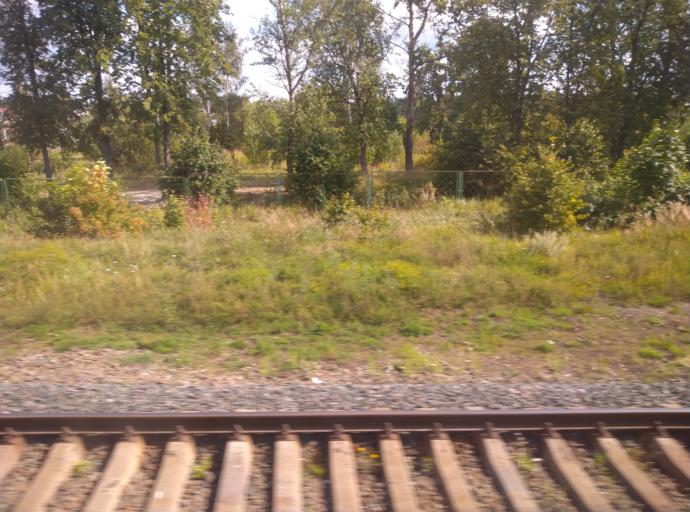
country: RU
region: Leningrad
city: Ul'yanovka
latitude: 59.6282
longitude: 30.7668
